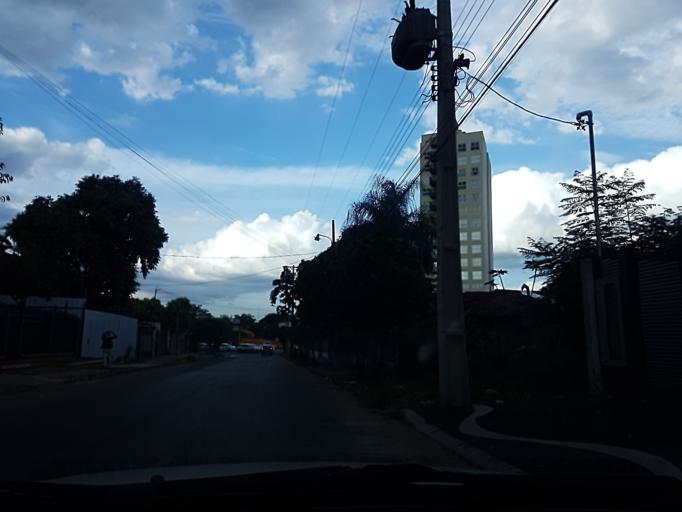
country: PY
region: Central
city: Fernando de la Mora
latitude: -25.2918
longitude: -57.5530
